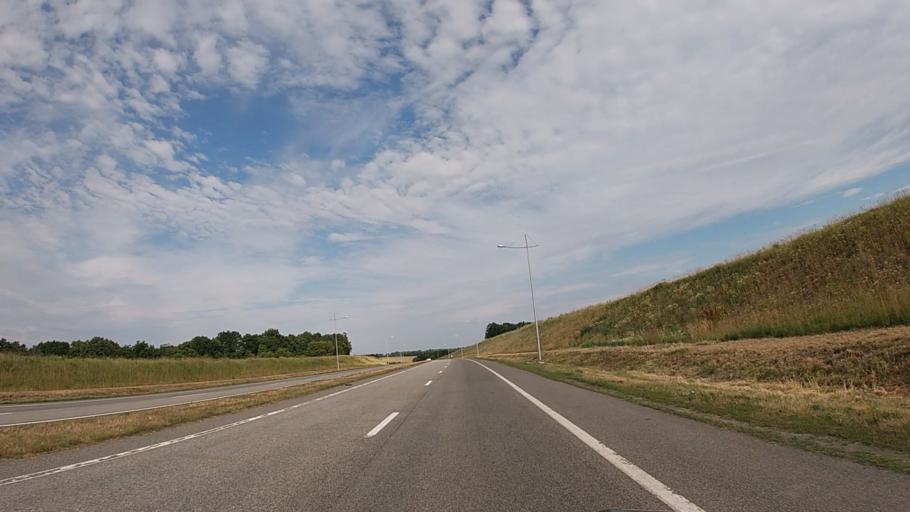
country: RU
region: Belgorod
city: Tomarovka
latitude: 50.7059
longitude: 36.2154
